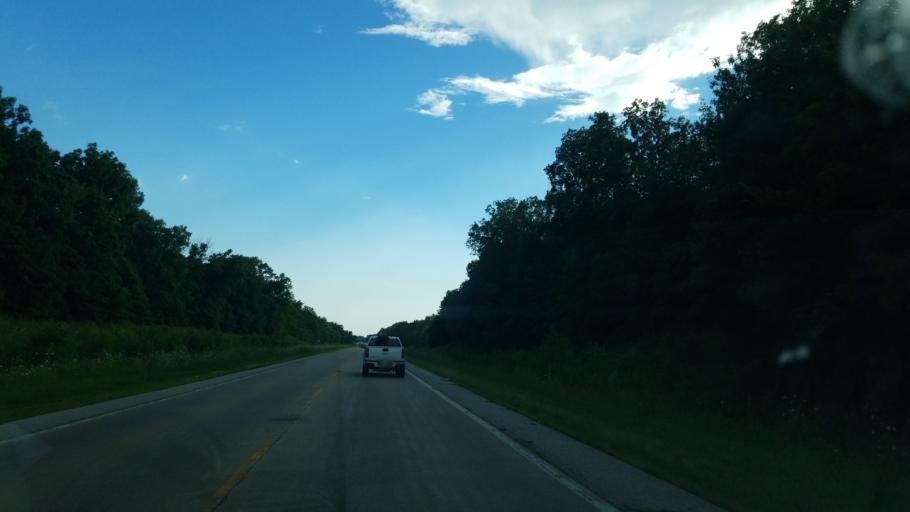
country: US
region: Illinois
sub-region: Marion County
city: Central City
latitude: 38.5680
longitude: -89.1137
